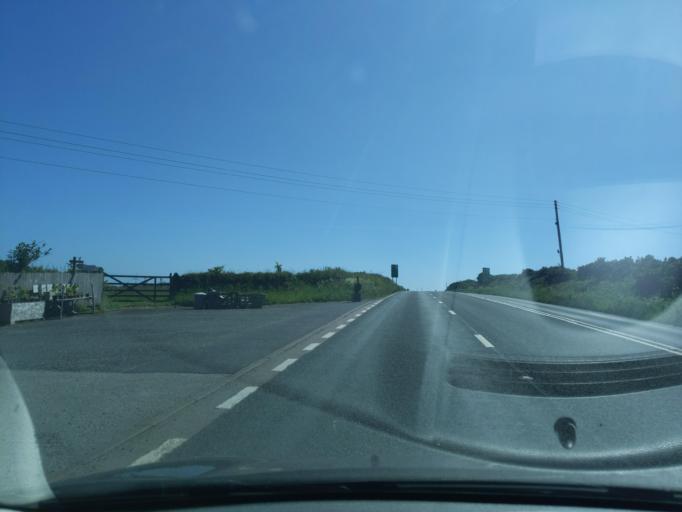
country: GB
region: England
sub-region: Cornwall
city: Wendron
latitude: 50.1437
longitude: -5.2148
